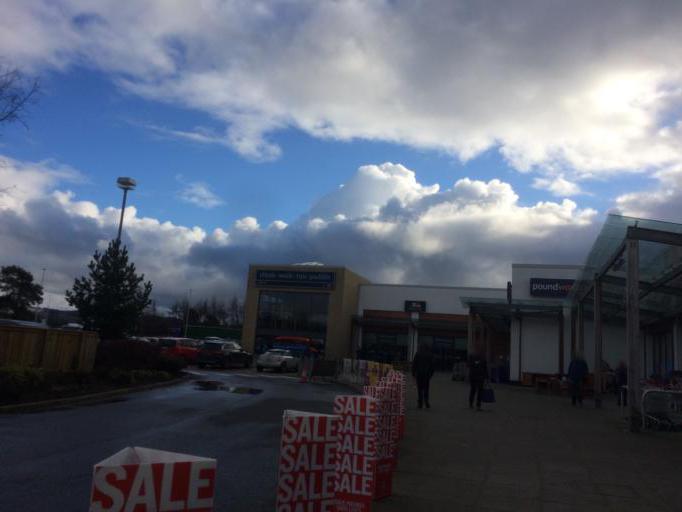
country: GB
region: Scotland
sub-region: Perth and Kinross
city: Luncarty
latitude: 56.4192
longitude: -3.4680
